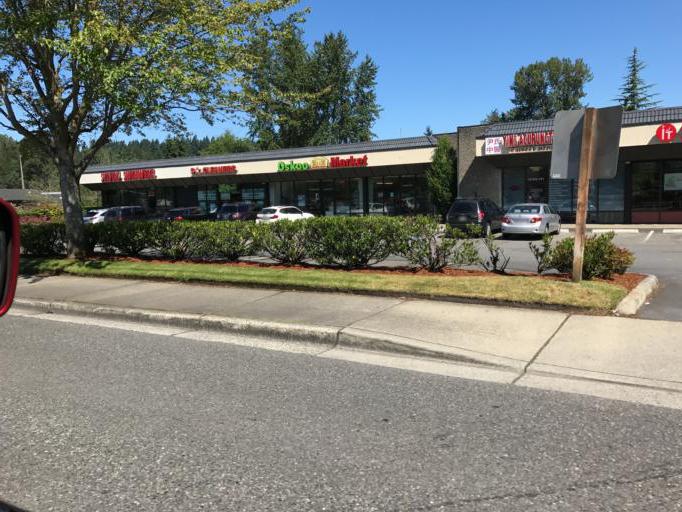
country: US
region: Washington
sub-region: King County
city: Bellevue
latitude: 47.6280
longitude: -122.1520
